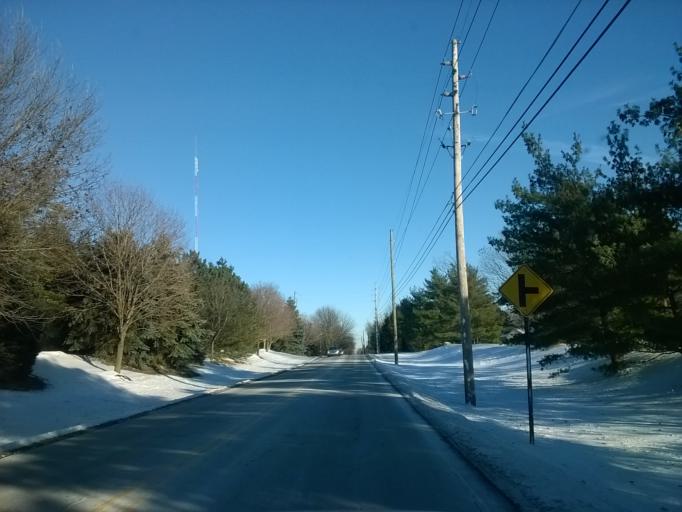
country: US
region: Indiana
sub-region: Marion County
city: Meridian Hills
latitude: 39.9267
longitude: -86.1909
